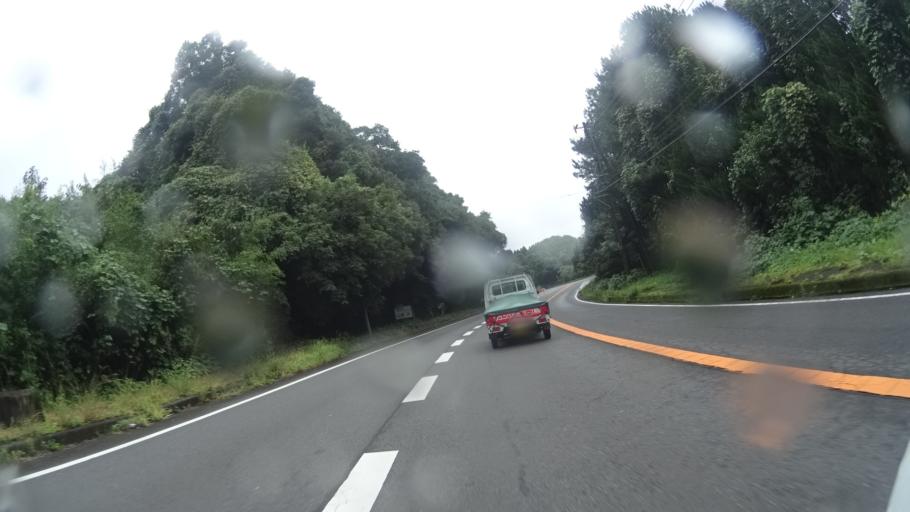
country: JP
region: Kagoshima
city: Kajiki
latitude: 31.7764
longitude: 130.6698
